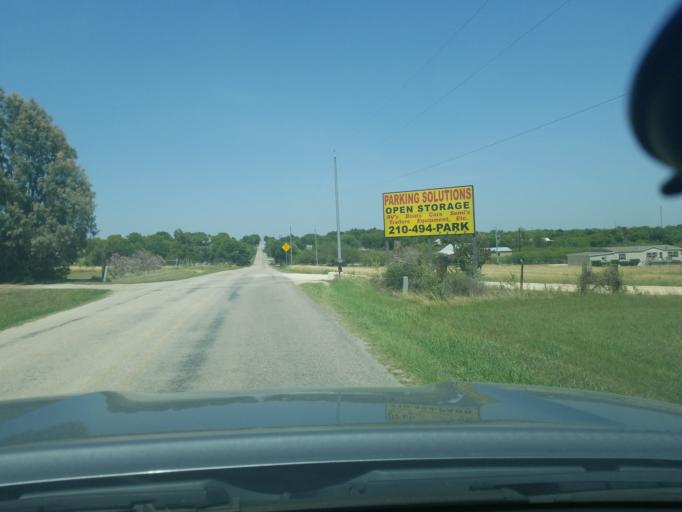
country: US
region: Texas
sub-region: Guadalupe County
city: Cibolo
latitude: 29.5831
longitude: -98.2092
